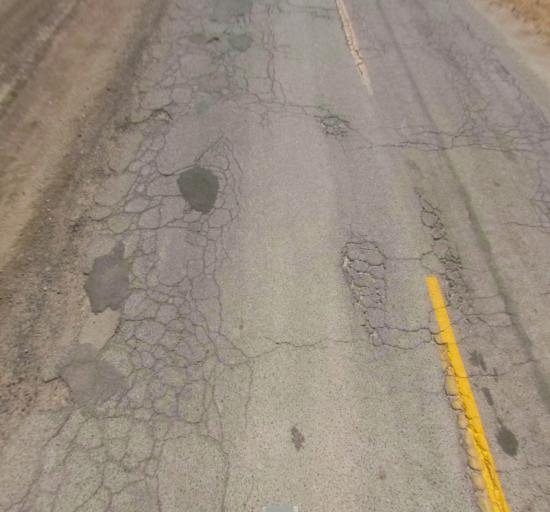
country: US
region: California
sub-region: Fresno County
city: Mendota
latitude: 36.8366
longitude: -120.2227
